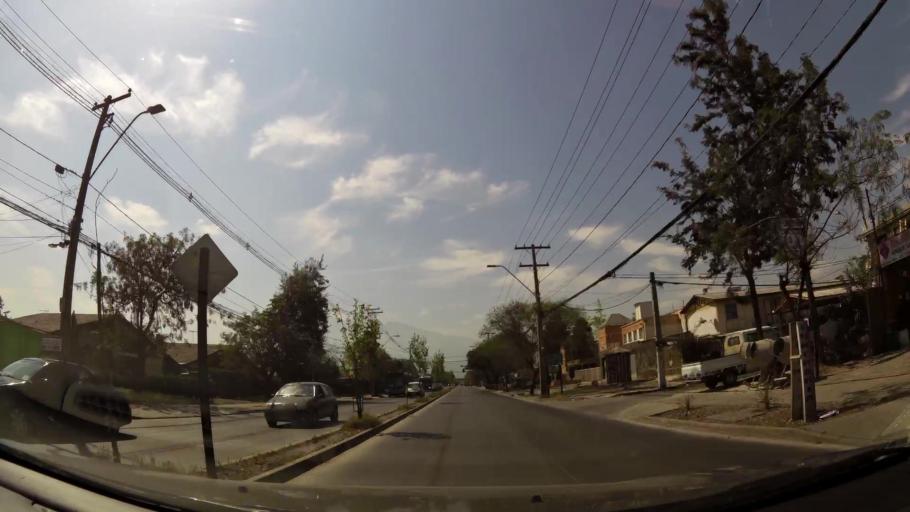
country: CL
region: Santiago Metropolitan
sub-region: Provincia de Cordillera
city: Puente Alto
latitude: -33.5802
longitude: -70.5889
